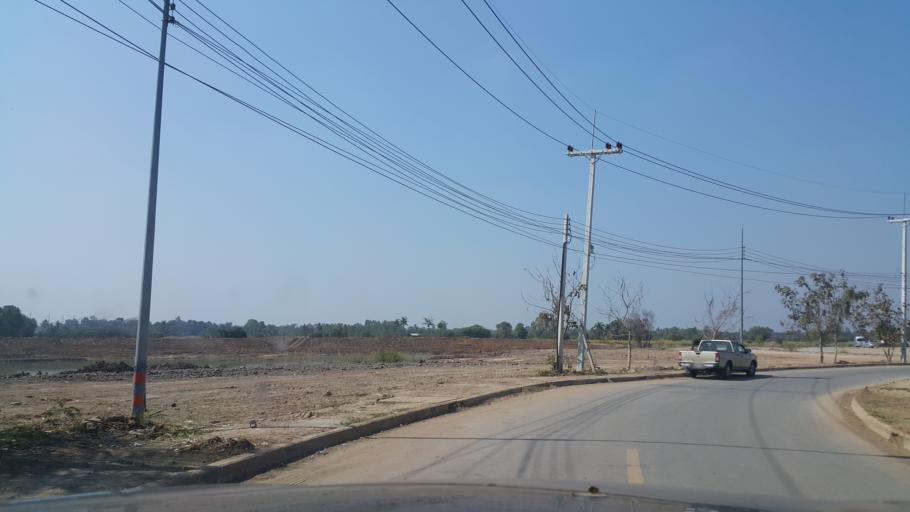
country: TH
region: Khon Kaen
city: Khon Kaen
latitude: 16.5110
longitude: 102.8682
